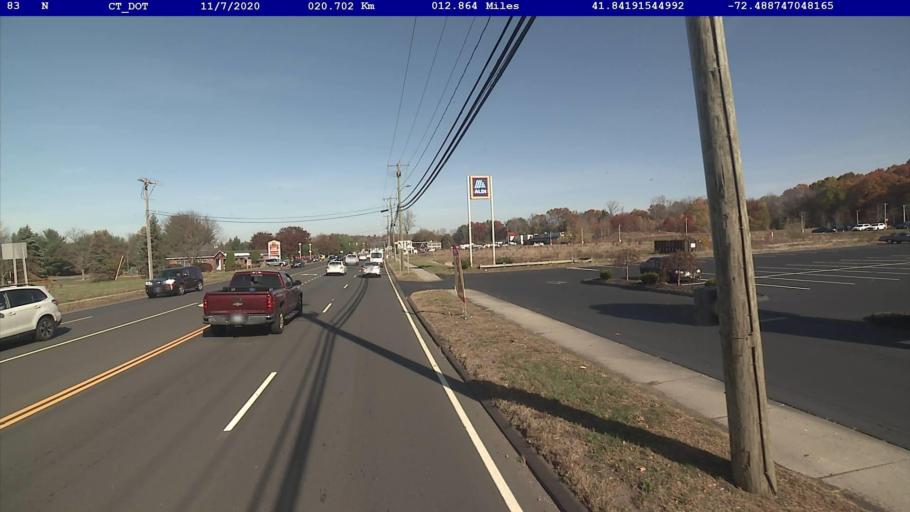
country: US
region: Connecticut
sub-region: Tolland County
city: Rockville
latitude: 41.8419
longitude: -72.4887
